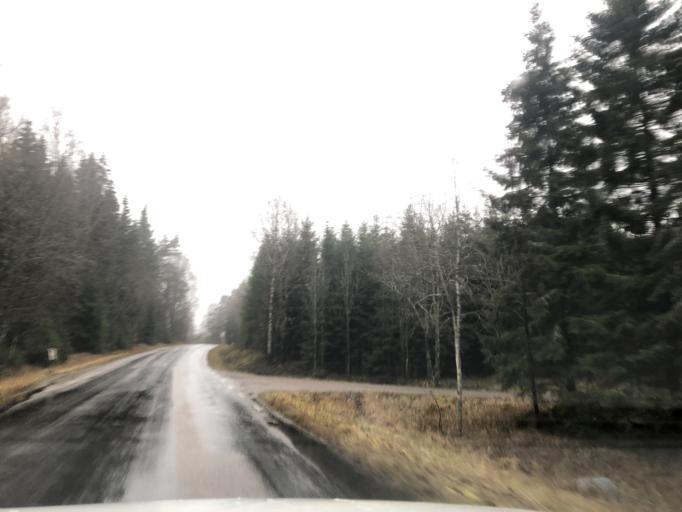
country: SE
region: Vaestra Goetaland
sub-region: Ulricehamns Kommun
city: Ulricehamn
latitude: 57.8376
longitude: 13.5342
